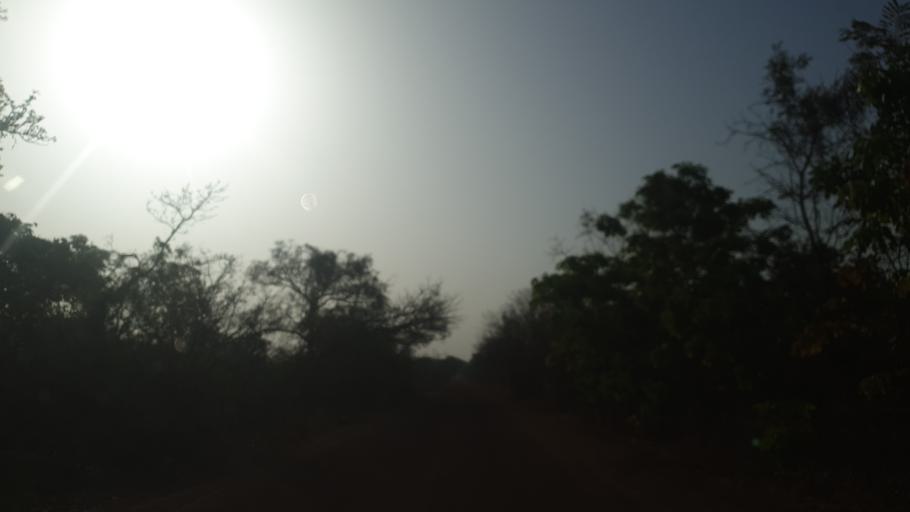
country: ML
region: Sikasso
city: Kolondieba
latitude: 10.8973
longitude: -6.8870
